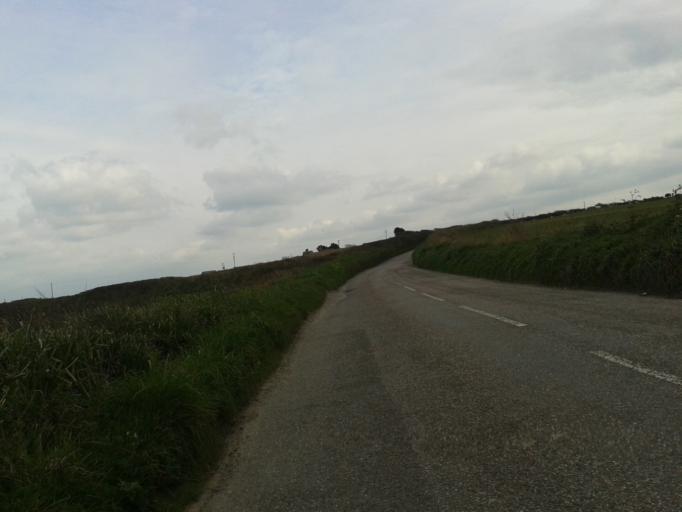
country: GB
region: England
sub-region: Devon
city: Braunton
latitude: 51.1827
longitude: -4.1879
